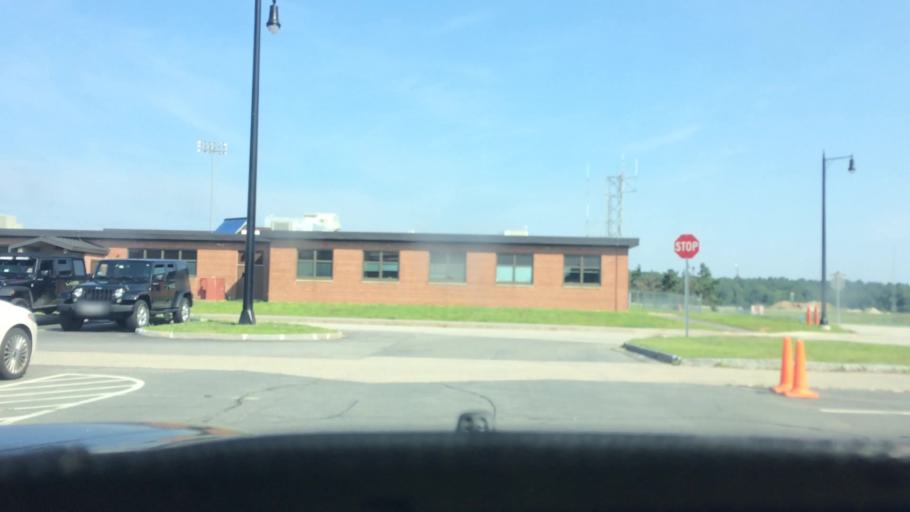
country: US
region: Maine
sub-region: York County
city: South Eliot
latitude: 43.0892
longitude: -70.8195
